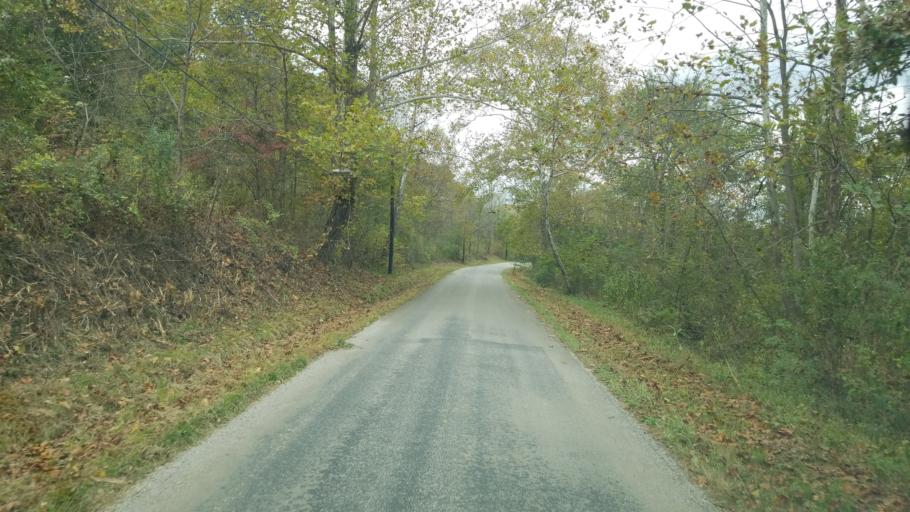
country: US
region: Ohio
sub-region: Jackson County
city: Wellston
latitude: 39.1587
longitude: -82.5794
